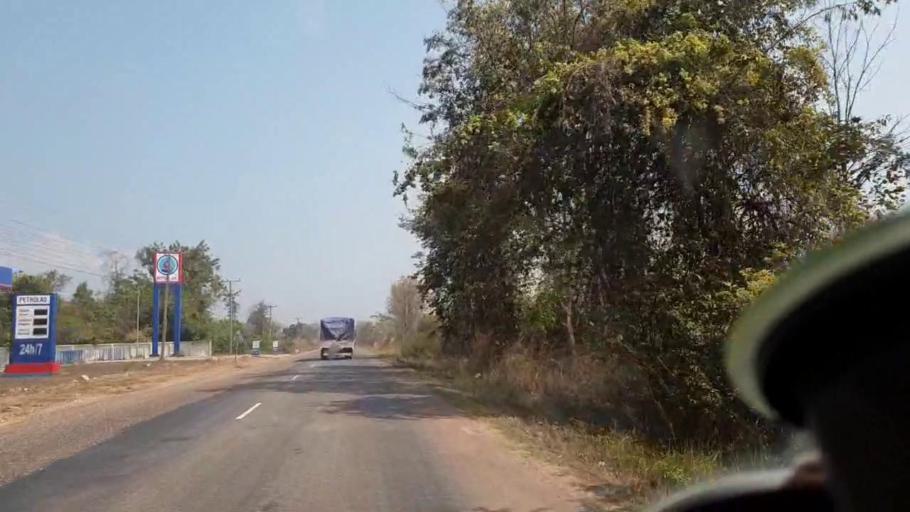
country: TH
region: Nong Khai
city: Phon Phisai
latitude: 18.0973
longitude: 103.0171
